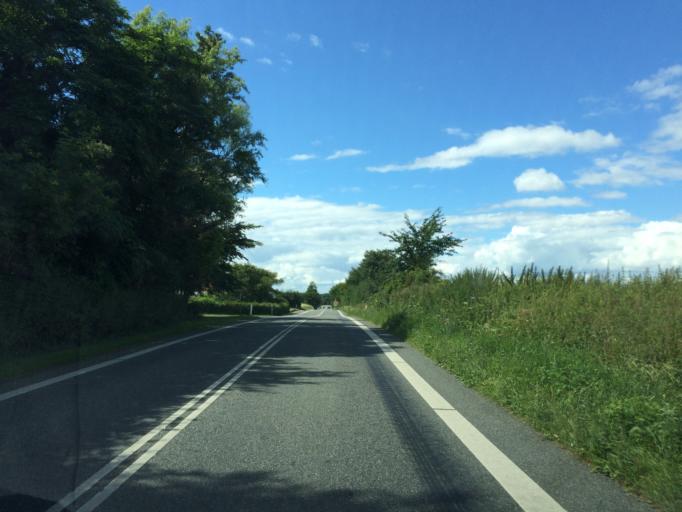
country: DK
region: South Denmark
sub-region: Faaborg-Midtfyn Kommune
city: Faaborg
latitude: 55.1383
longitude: 10.1756
